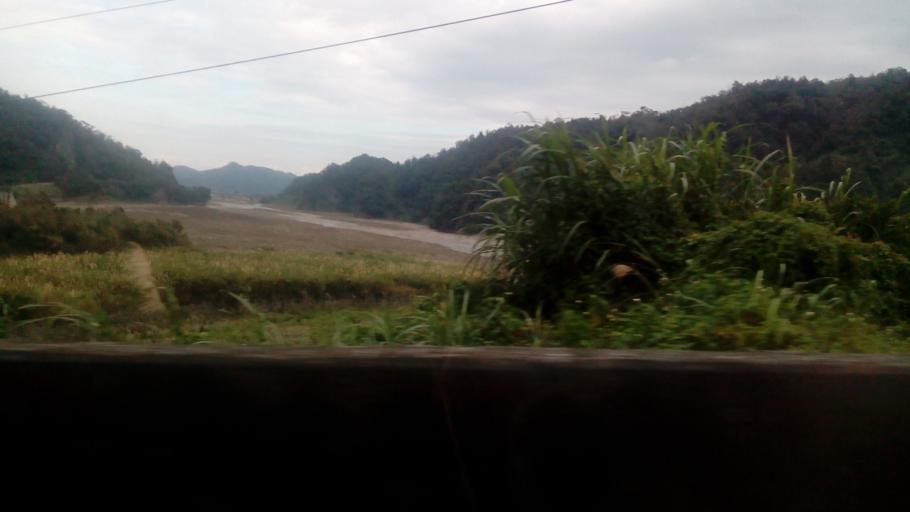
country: TW
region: Taiwan
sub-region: Yilan
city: Yilan
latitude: 24.6372
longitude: 121.5541
